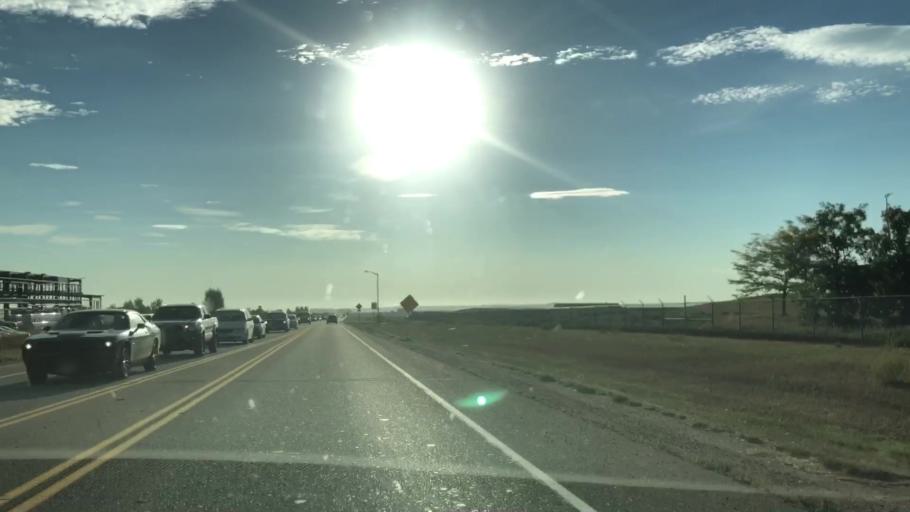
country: US
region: Colorado
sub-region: Weld County
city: Windsor
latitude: 40.4360
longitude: -104.9660
